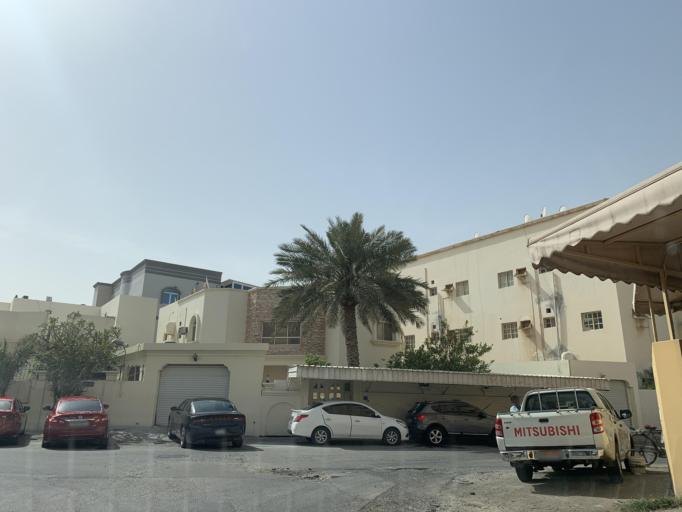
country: BH
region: Northern
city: Madinat `Isa
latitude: 26.1715
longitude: 50.5644
